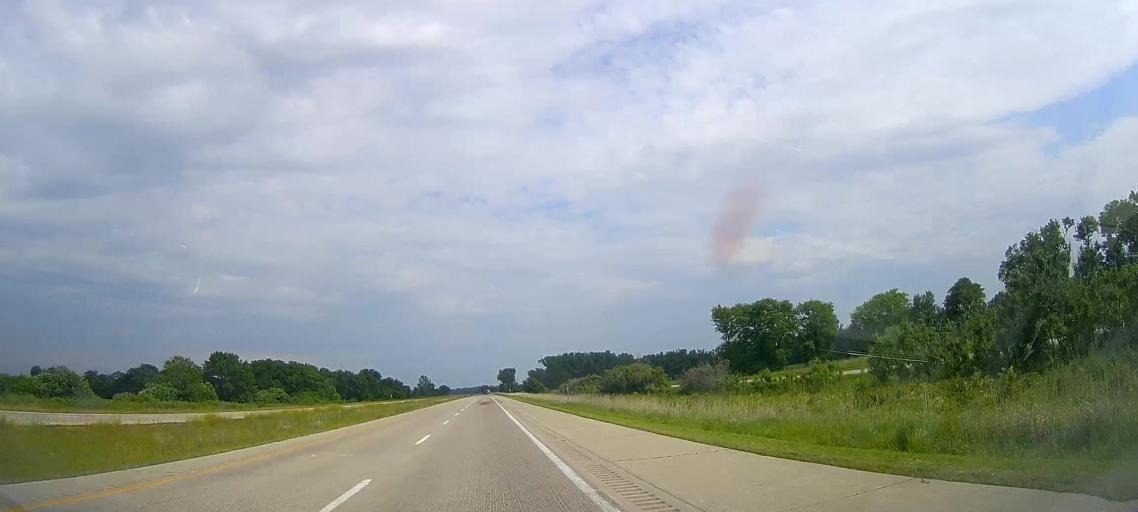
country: US
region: Nebraska
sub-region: Burt County
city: Tekamah
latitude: 41.8436
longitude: -96.0922
